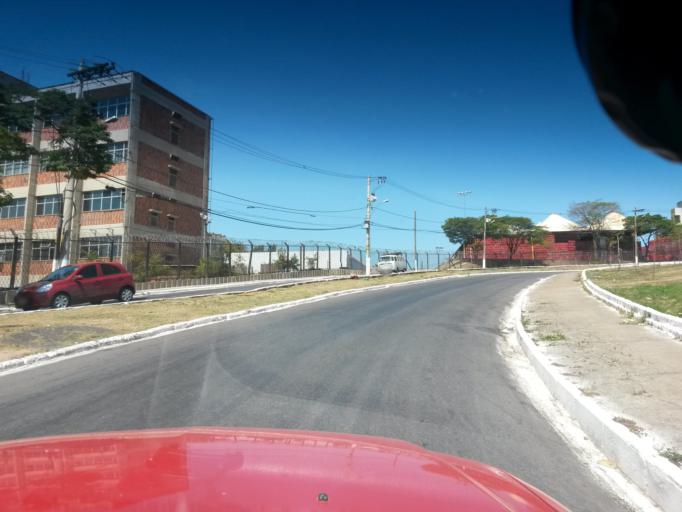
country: BR
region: Minas Gerais
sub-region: Belo Horizonte
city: Belo Horizonte
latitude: -19.8869
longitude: -43.9682
